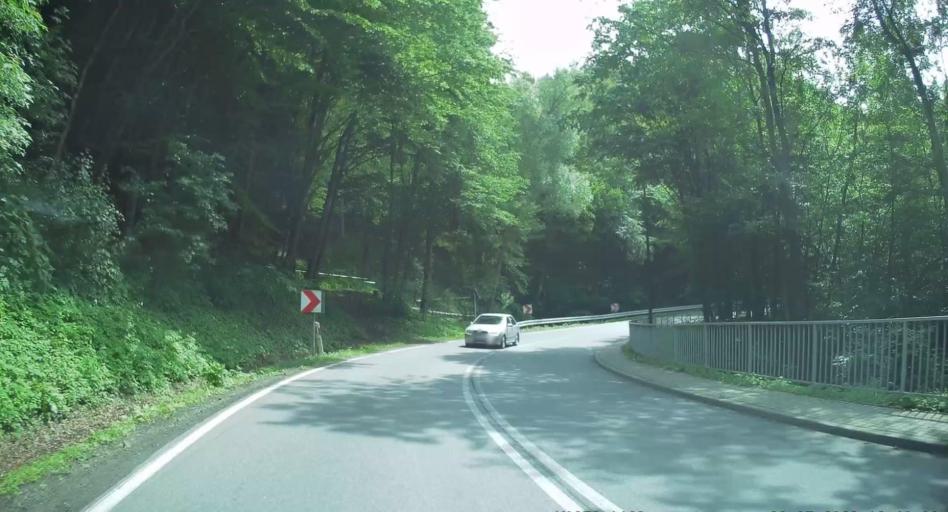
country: PL
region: Lesser Poland Voivodeship
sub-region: Powiat nowosadecki
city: Muszyna
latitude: 49.3532
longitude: 20.8122
